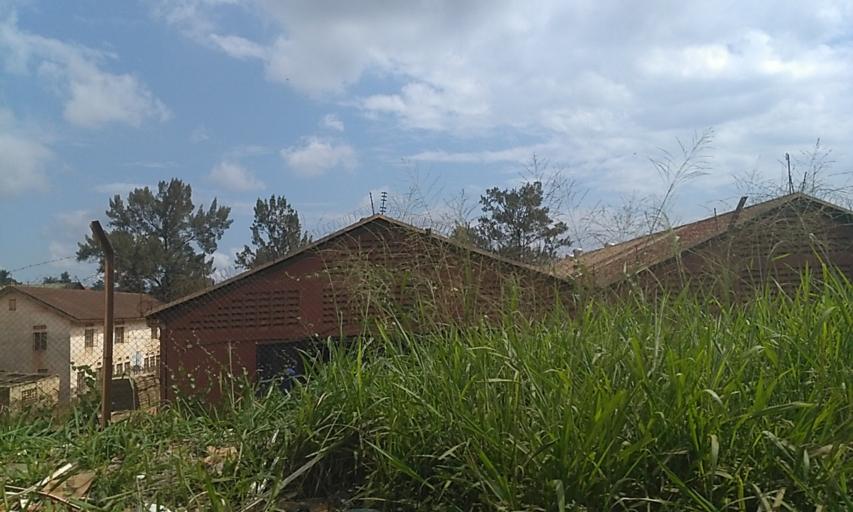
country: UG
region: Central Region
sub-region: Wakiso District
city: Kireka
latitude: 0.3394
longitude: 32.6180
